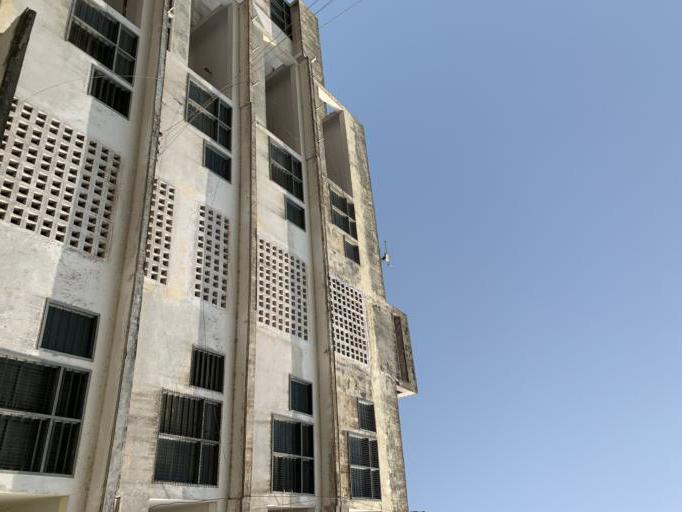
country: GH
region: Central
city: Winneba
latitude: 5.3373
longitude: -0.6303
